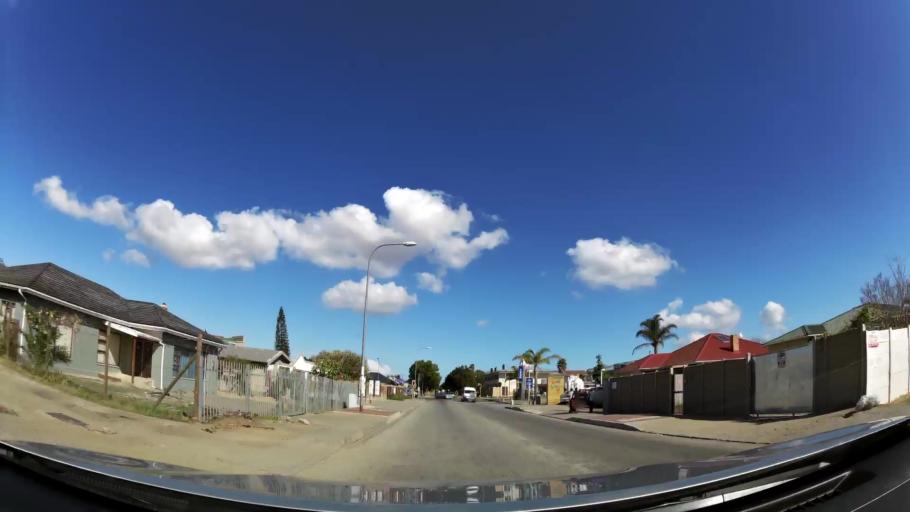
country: ZA
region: Western Cape
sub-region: Eden District Municipality
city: George
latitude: -33.9659
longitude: 22.4585
